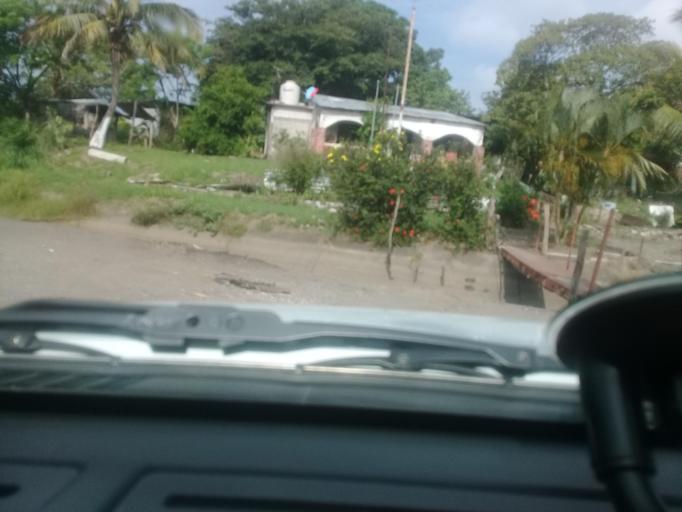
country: MX
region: Veracruz
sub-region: Paso de Ovejas
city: Tolome
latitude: 19.2636
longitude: -96.3737
